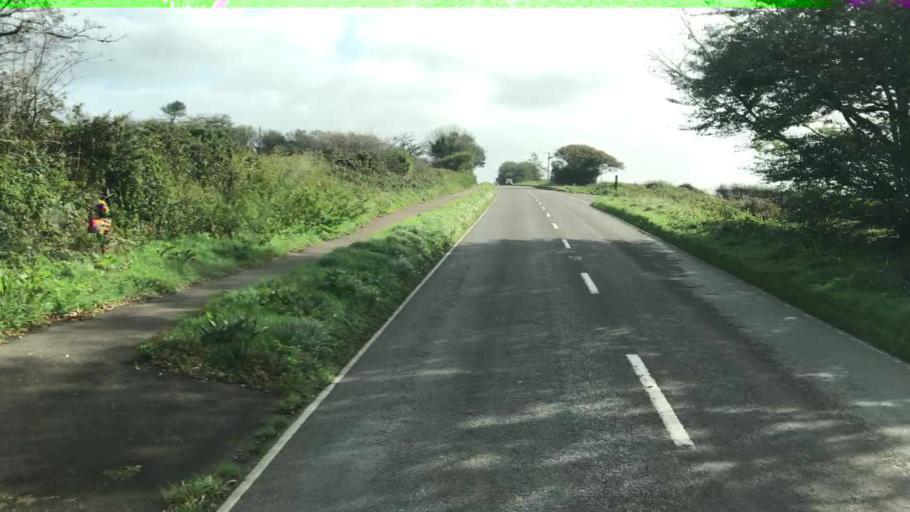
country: GB
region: England
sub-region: Cornwall
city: Gunnislake
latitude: 50.5165
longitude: -4.2632
